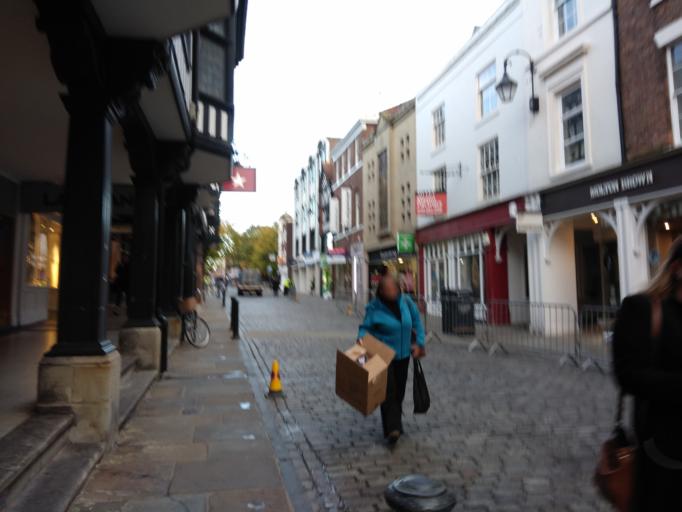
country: GB
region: England
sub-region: Cheshire West and Chester
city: Chester
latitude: 53.1910
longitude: -2.8916
